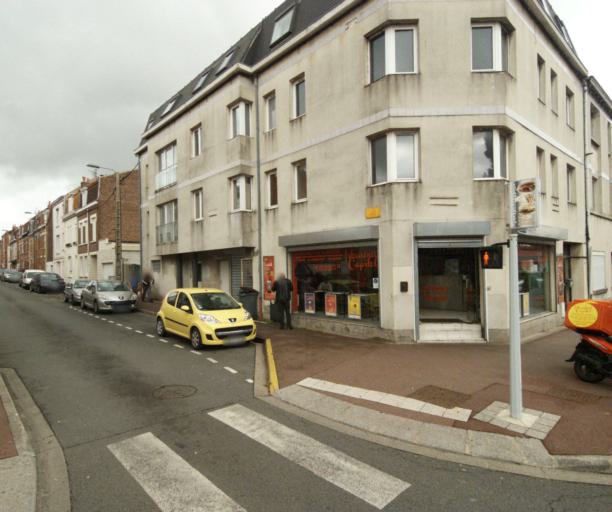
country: FR
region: Nord-Pas-de-Calais
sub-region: Departement du Nord
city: Lomme
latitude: 50.6467
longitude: 2.9985
